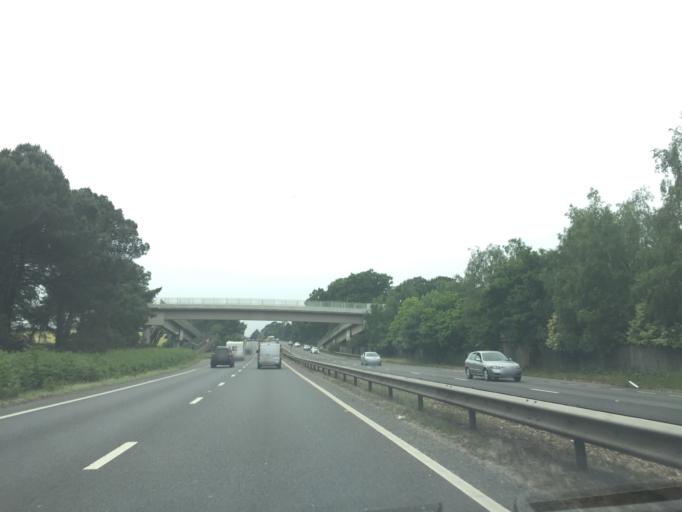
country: GB
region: England
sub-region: Dorset
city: St Leonards
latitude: 50.8338
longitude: -1.8269
